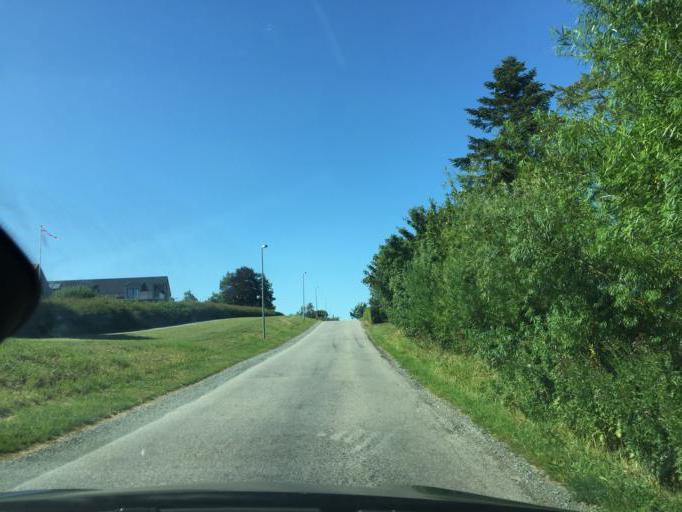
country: DK
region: South Denmark
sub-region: Nordfyns Kommune
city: Sonderso
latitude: 55.4834
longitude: 10.2640
